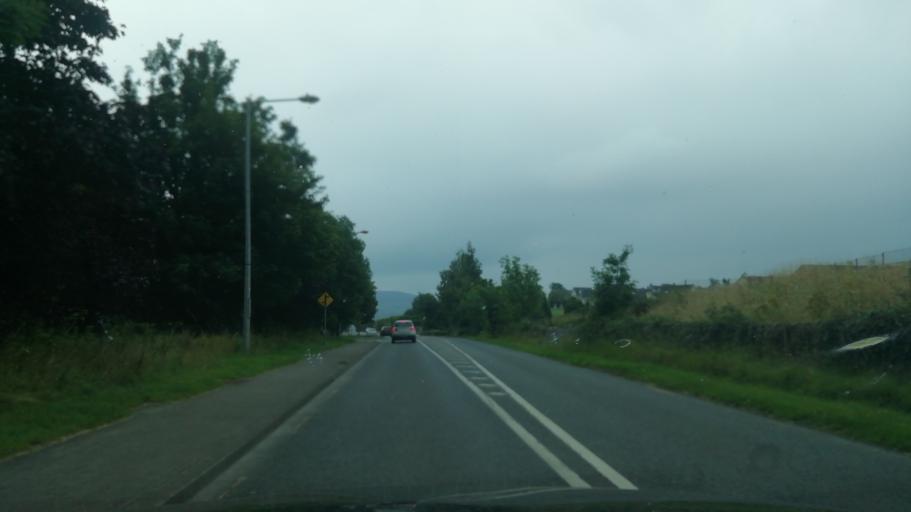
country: IE
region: Munster
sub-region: South Tipperary
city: Cluain Meala
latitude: 52.3725
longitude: -7.6992
